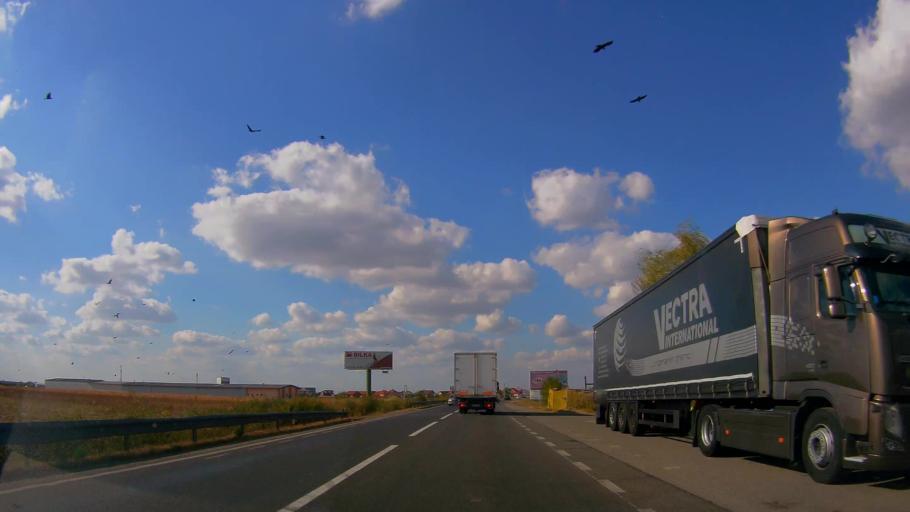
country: RO
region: Satu Mare
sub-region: Oras Ardud
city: Madaras
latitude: 47.7269
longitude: 22.8847
